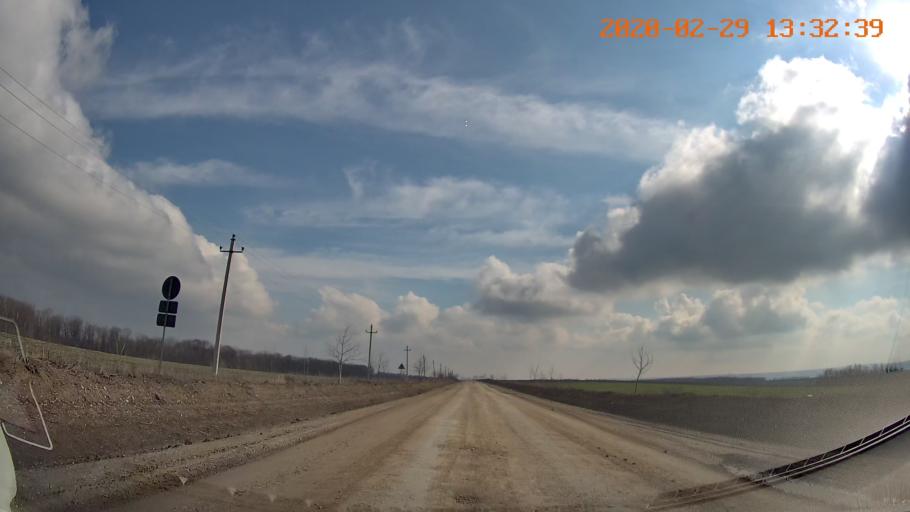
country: MD
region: Telenesti
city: Camenca
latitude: 47.8780
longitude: 28.6112
